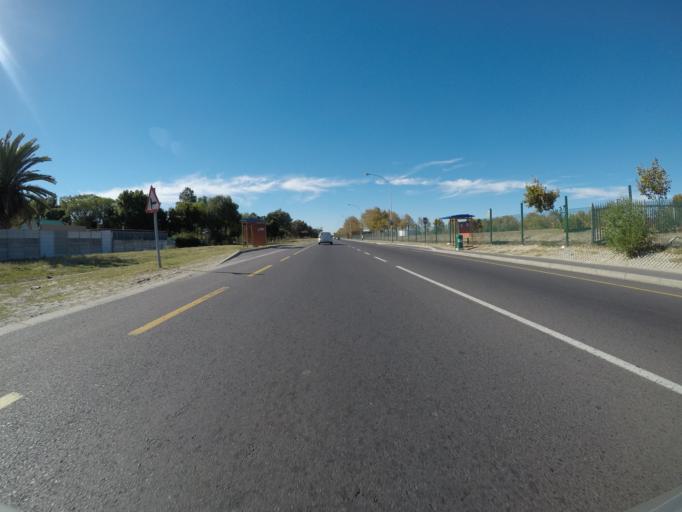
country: ZA
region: Western Cape
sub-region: City of Cape Town
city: Kraaifontein
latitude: -33.9416
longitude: 18.6768
